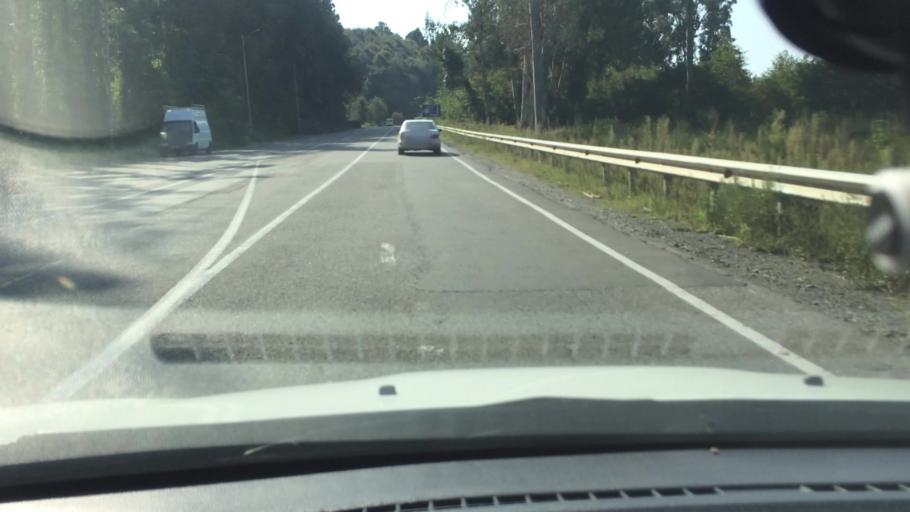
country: GE
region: Guria
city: Urek'i
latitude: 41.9725
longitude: 41.7821
